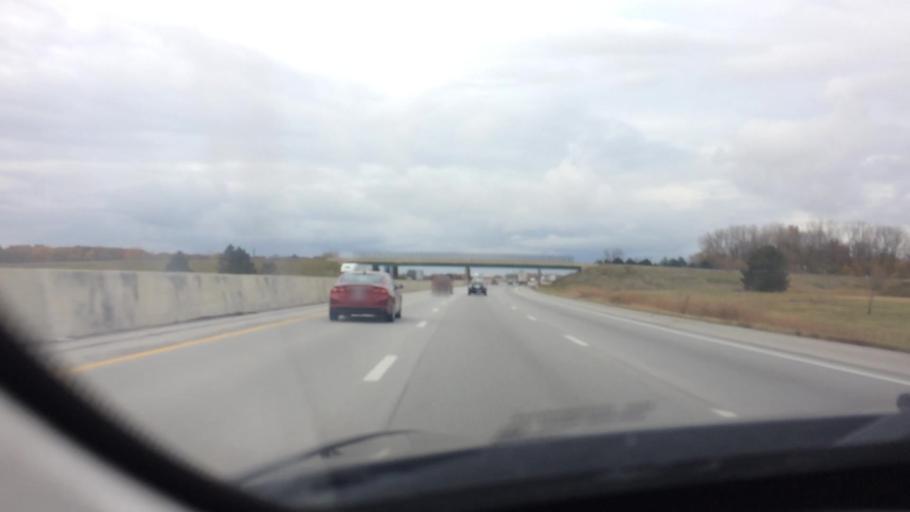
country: US
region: Ohio
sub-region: Wood County
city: North Baltimore
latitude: 41.2382
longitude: -83.6537
